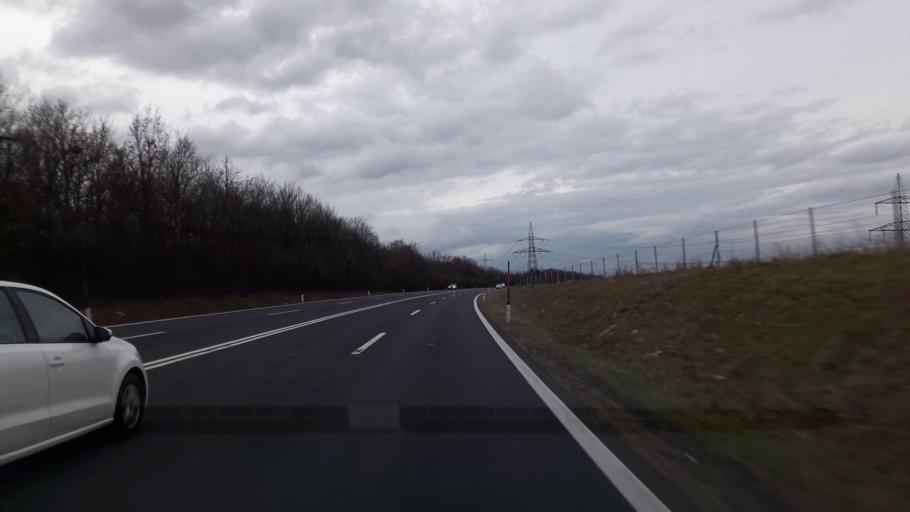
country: AT
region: Burgenland
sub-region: Politischer Bezirk Mattersburg
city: Mattersburg
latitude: 47.7339
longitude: 16.3718
